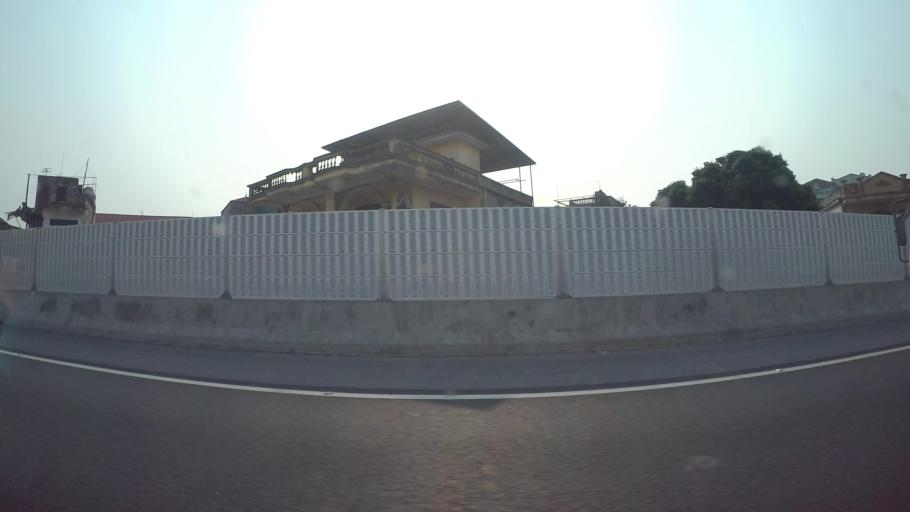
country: VN
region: Ha Noi
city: Van Dien
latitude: 20.9240
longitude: 105.8599
